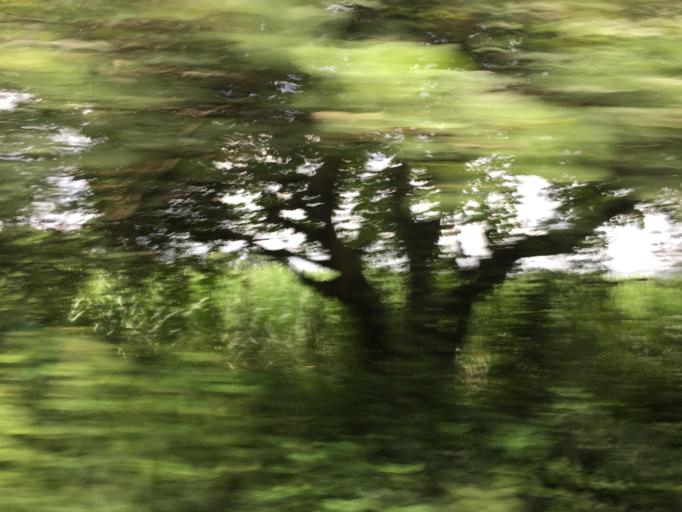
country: GT
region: Guatemala
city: Villa Canales
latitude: 14.4482
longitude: -90.5273
